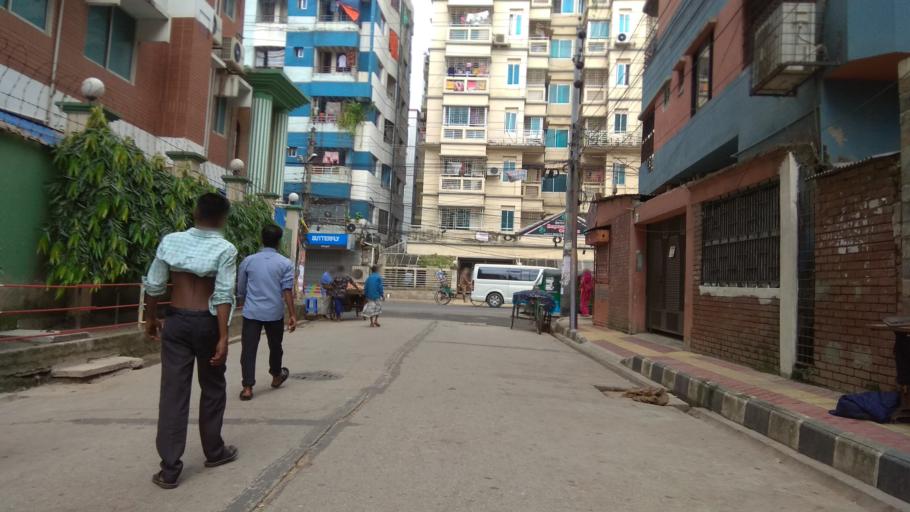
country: BD
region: Dhaka
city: Azimpur
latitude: 23.8122
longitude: 90.3571
